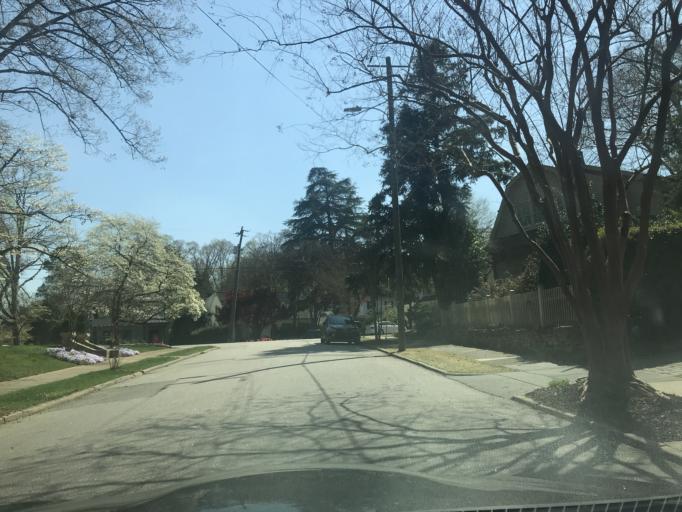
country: US
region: North Carolina
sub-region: Wake County
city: West Raleigh
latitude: 35.8124
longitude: -78.6428
